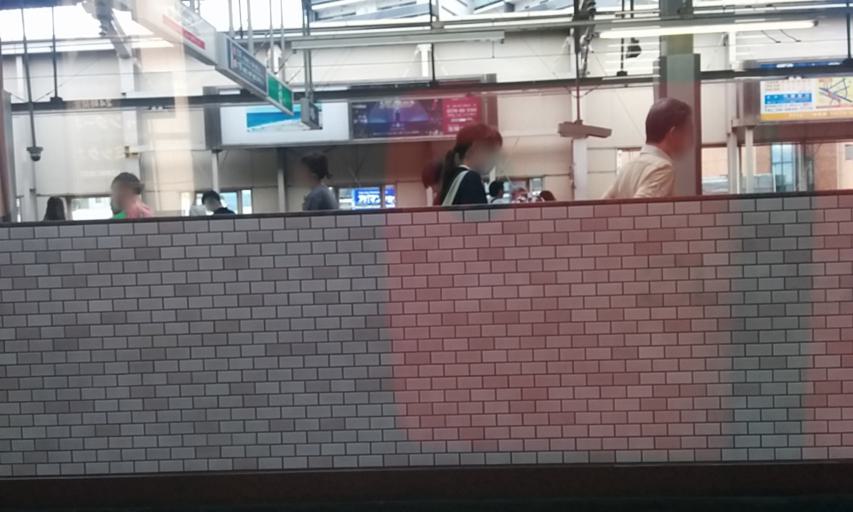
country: JP
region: Osaka
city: Toyonaka
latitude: 34.7875
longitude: 135.4609
